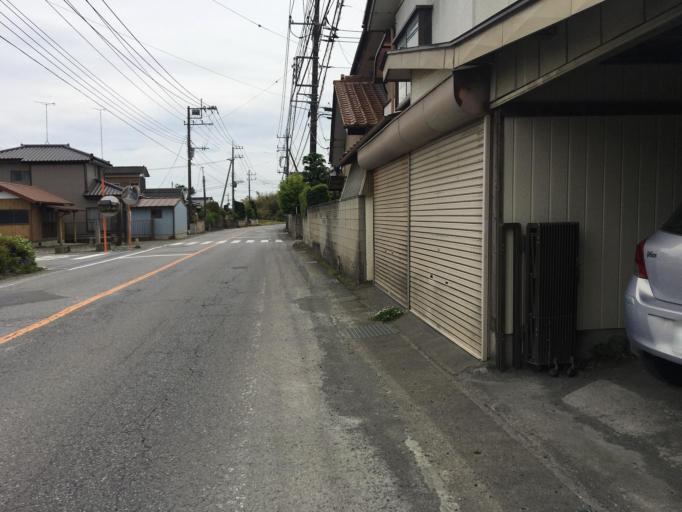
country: JP
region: Tochigi
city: Mibu
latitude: 36.4509
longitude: 139.7560
